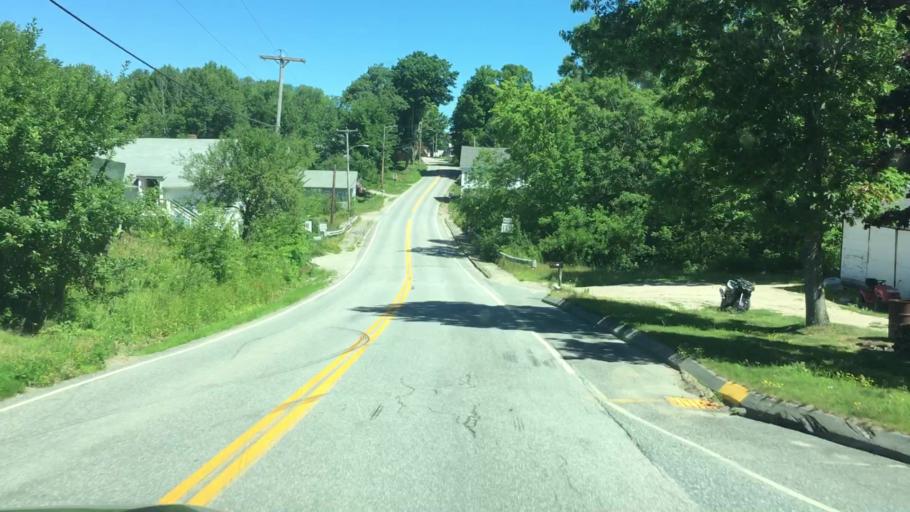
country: US
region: Maine
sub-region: Hancock County
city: Penobscot
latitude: 44.4519
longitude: -68.7027
